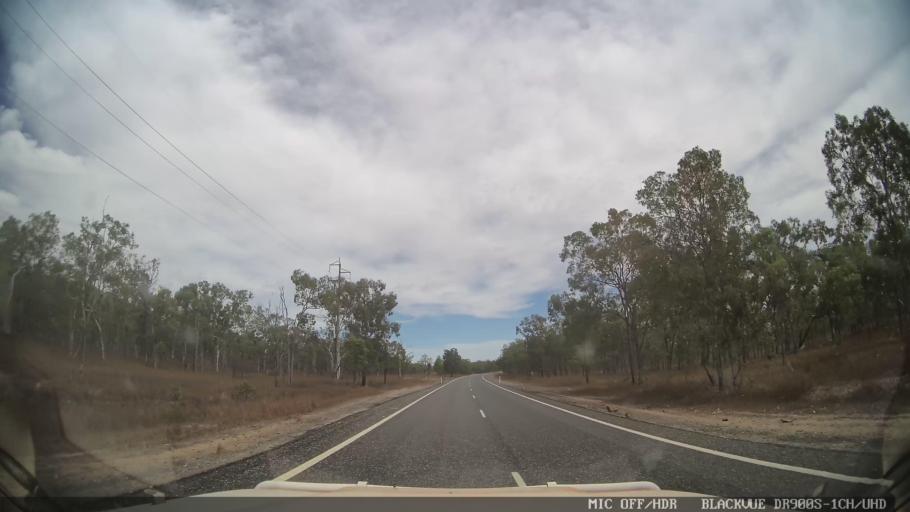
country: AU
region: Queensland
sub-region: Cairns
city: Port Douglas
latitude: -16.2506
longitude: 144.7261
